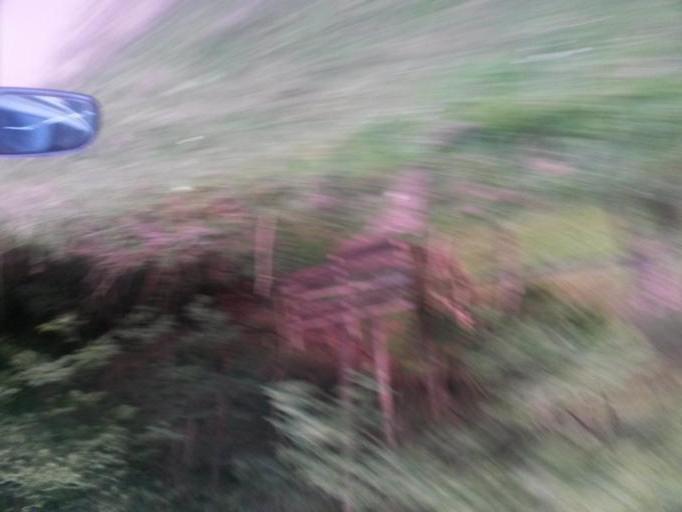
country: RO
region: Alba
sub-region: Comuna Ponor
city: Ponor
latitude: 46.3101
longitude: 23.4088
